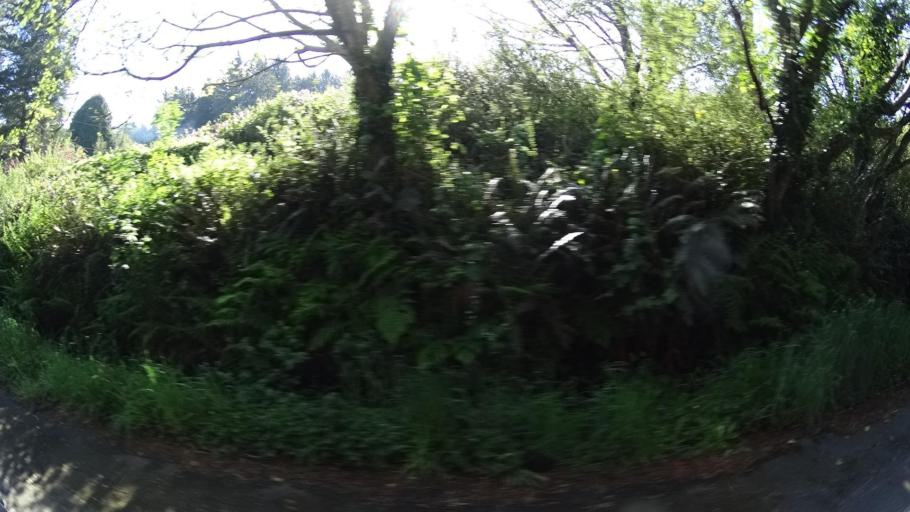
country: US
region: California
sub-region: Humboldt County
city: Westhaven-Moonstone
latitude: 41.1240
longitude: -124.1564
